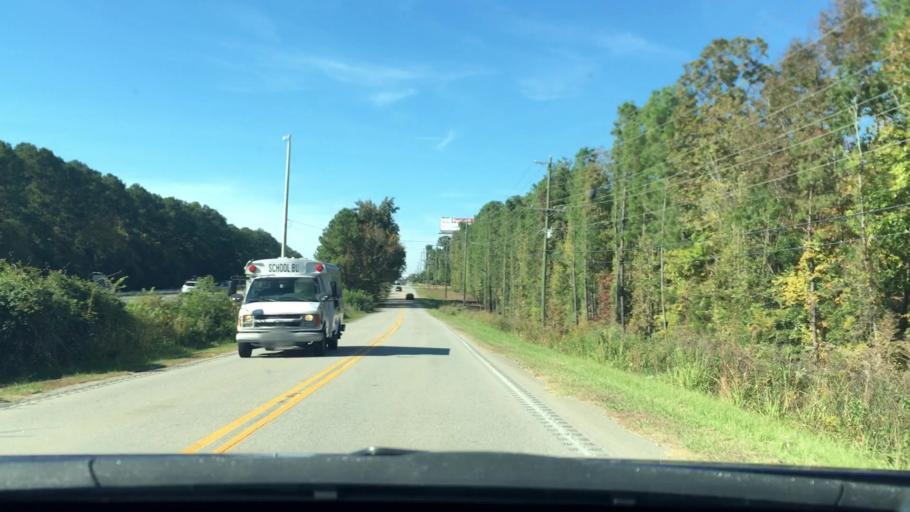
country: US
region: South Carolina
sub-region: Lexington County
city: Irmo
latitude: 34.1055
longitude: -81.1811
